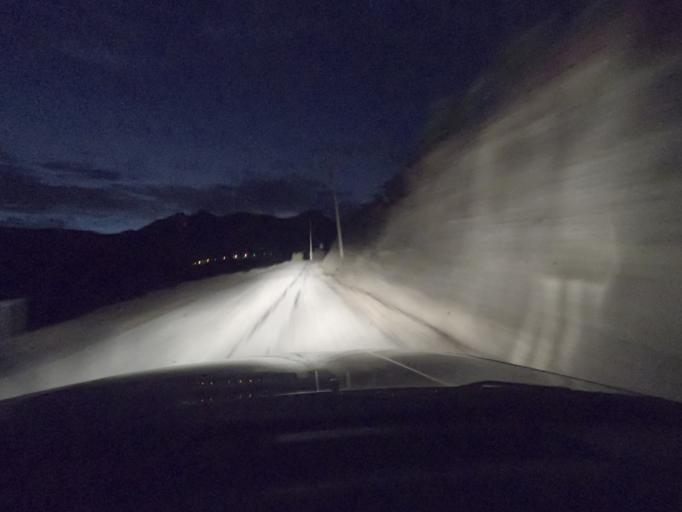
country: PT
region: Vila Real
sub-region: Santa Marta de Penaguiao
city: Santa Marta de Penaguiao
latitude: 41.2162
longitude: -7.8428
